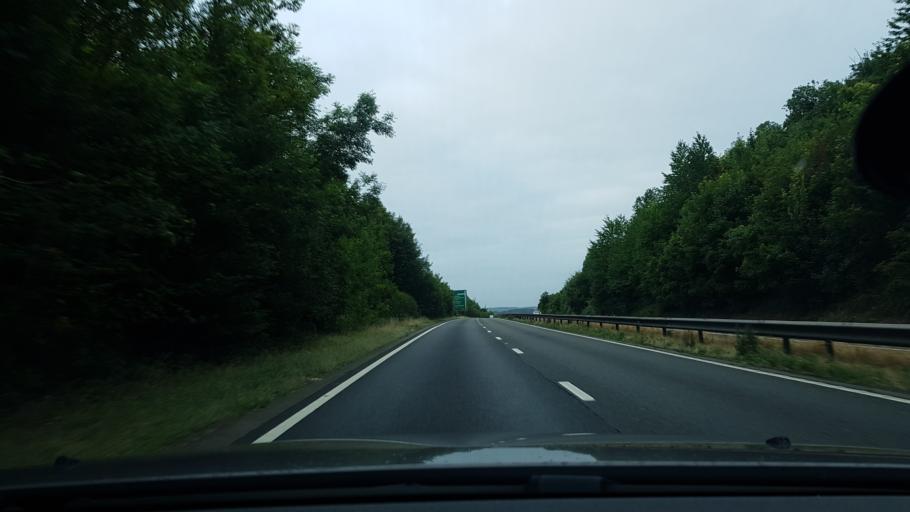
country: GB
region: England
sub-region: Hampshire
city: Overton
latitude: 51.1847
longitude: -1.3363
